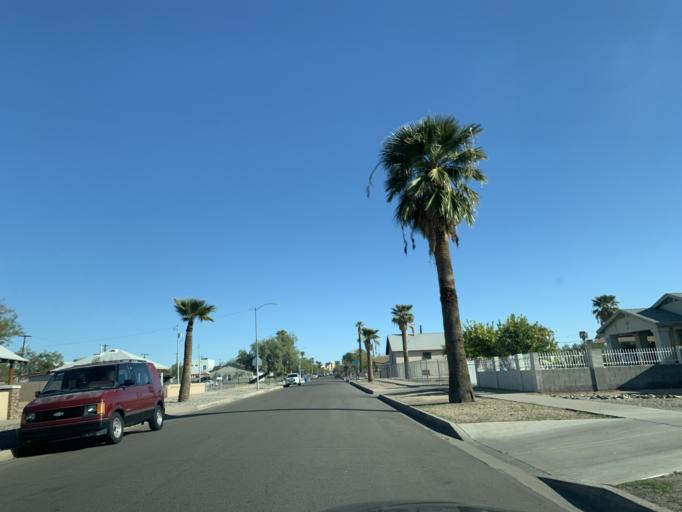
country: US
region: Arizona
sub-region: Maricopa County
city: Phoenix
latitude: 33.4549
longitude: -112.0616
